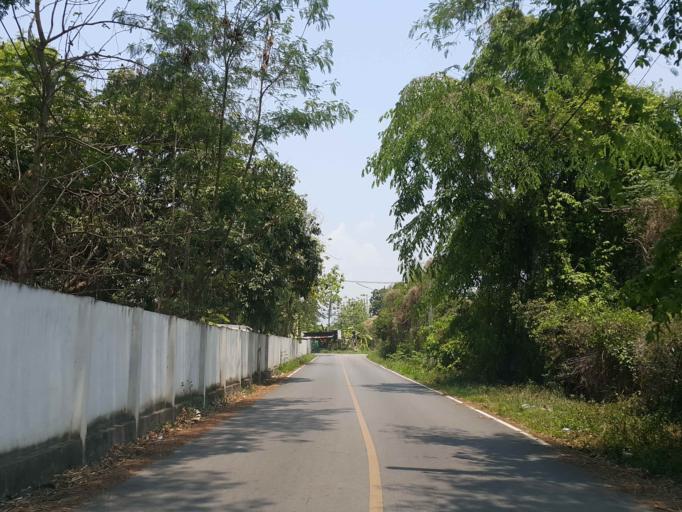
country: TH
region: Chiang Mai
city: San Kamphaeng
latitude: 18.7550
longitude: 99.0808
